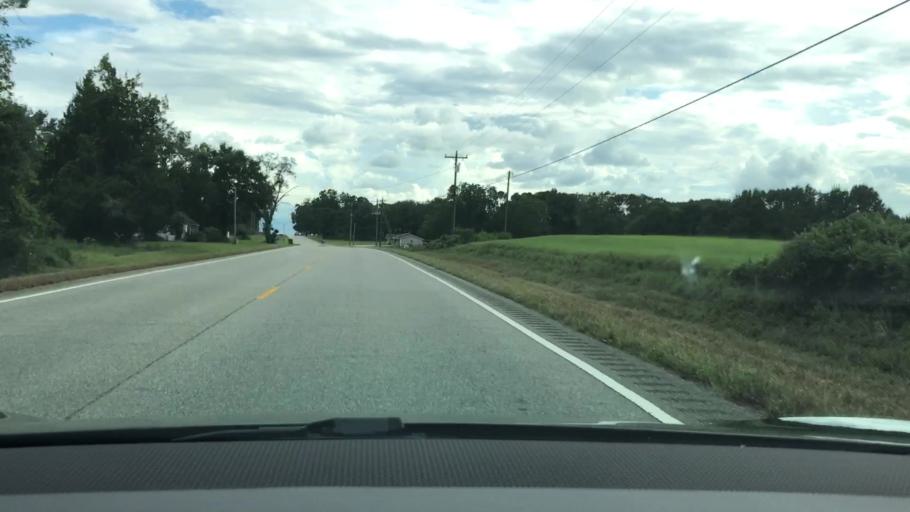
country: US
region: Alabama
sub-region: Pike County
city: Troy
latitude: 31.6689
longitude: -85.9590
